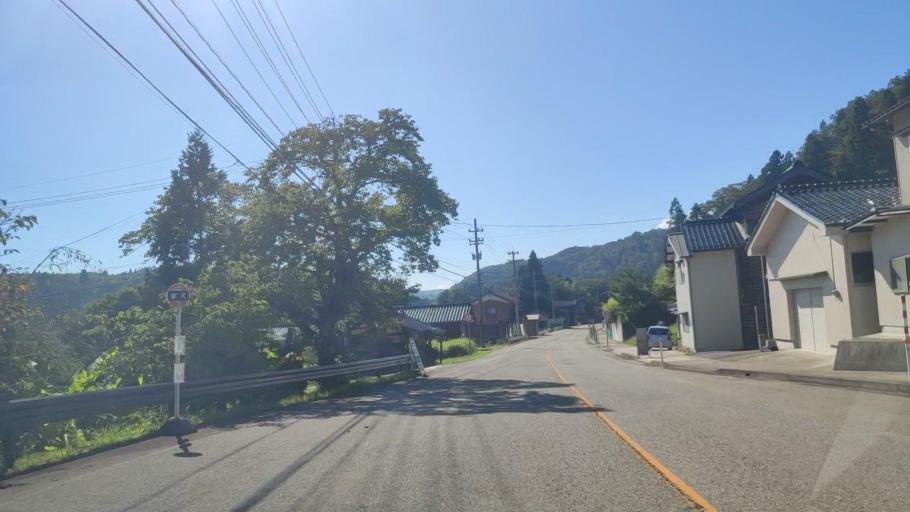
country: JP
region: Ishikawa
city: Nanao
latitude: 37.3404
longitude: 137.2255
